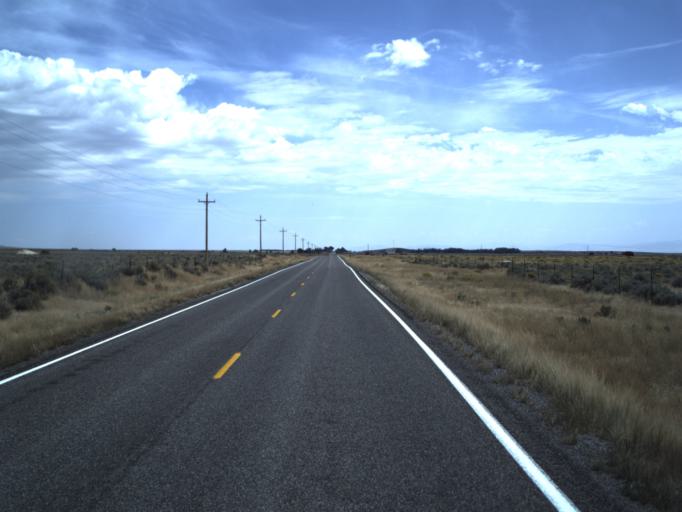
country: US
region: Idaho
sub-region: Cassia County
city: Burley
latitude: 41.8165
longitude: -113.3730
